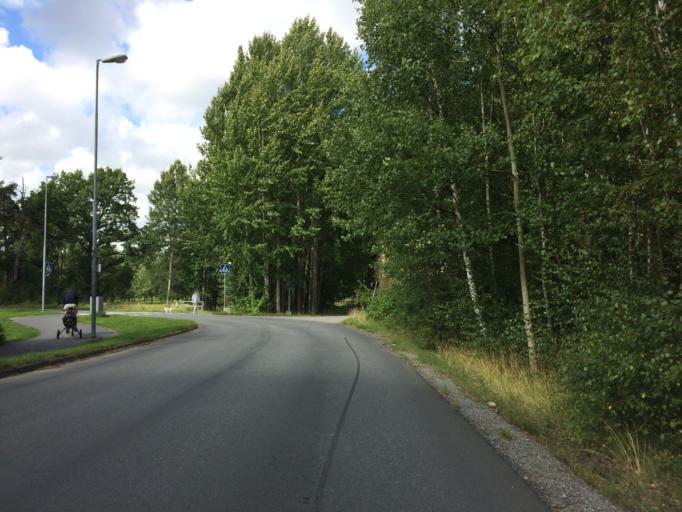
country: SE
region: Stockholm
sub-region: Upplands Vasby Kommun
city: Upplands Vaesby
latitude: 59.4654
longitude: 17.9092
